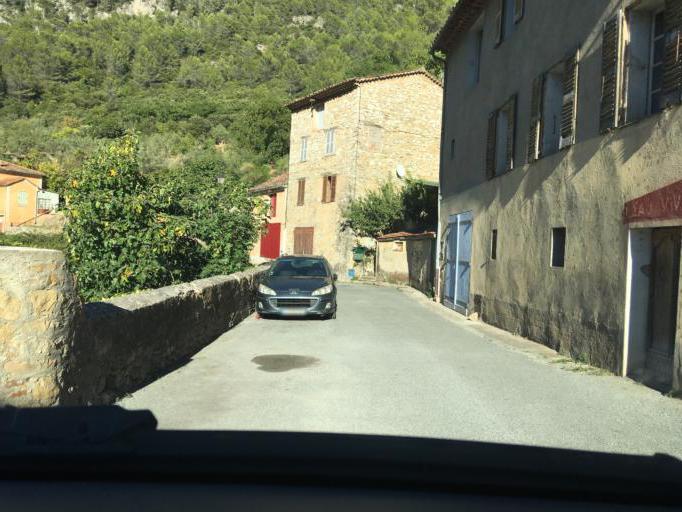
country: FR
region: Provence-Alpes-Cote d'Azur
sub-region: Departement du Var
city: Flayosc
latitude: 43.5761
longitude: 6.4249
